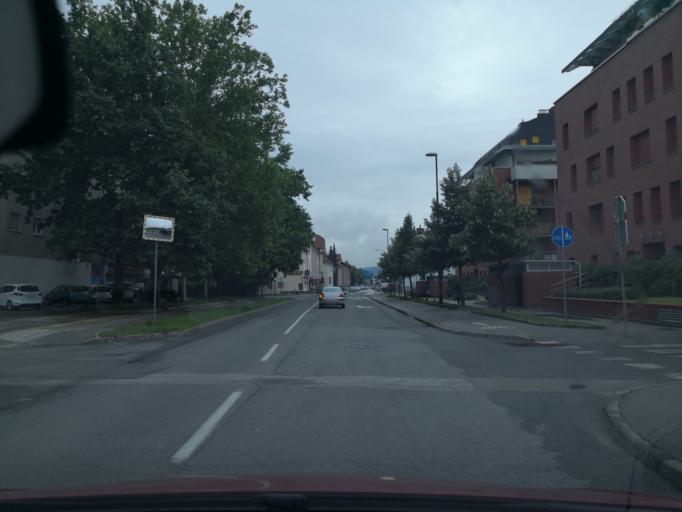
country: SI
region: Ljubljana
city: Ljubljana
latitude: 46.0639
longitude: 14.5308
